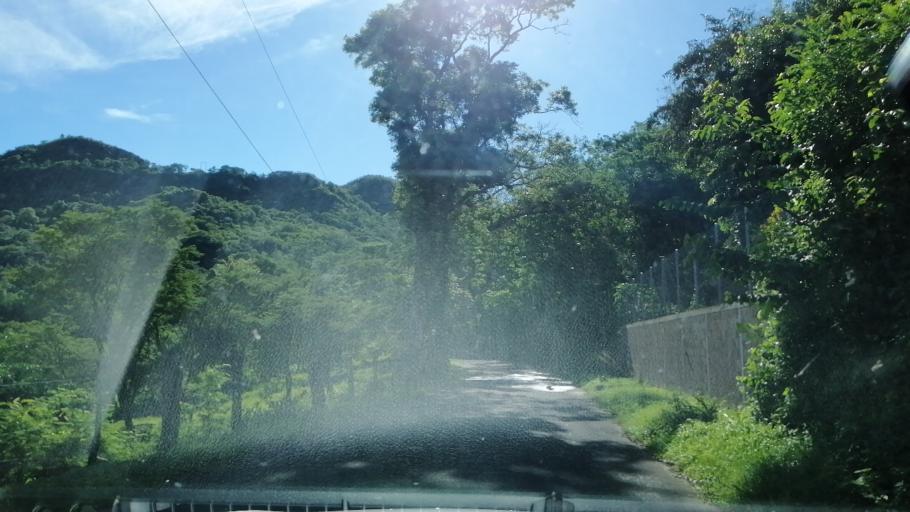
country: SV
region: Morazan
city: Corinto
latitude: 13.7900
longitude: -88.0259
